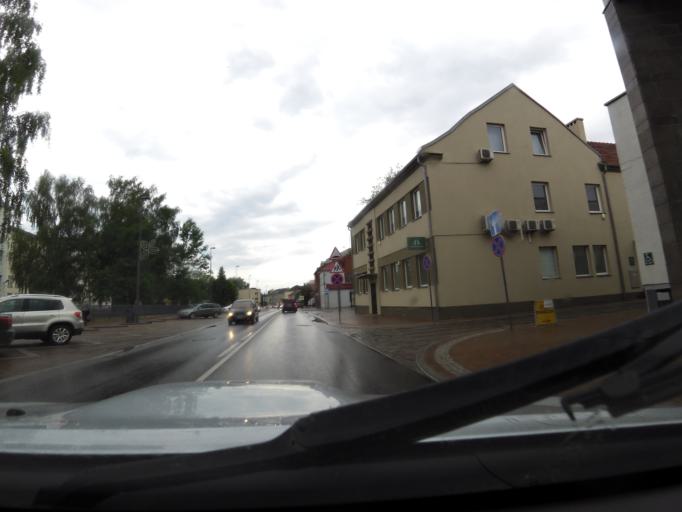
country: LT
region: Marijampoles apskritis
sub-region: Marijampole Municipality
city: Marijampole
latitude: 54.5548
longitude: 23.3530
